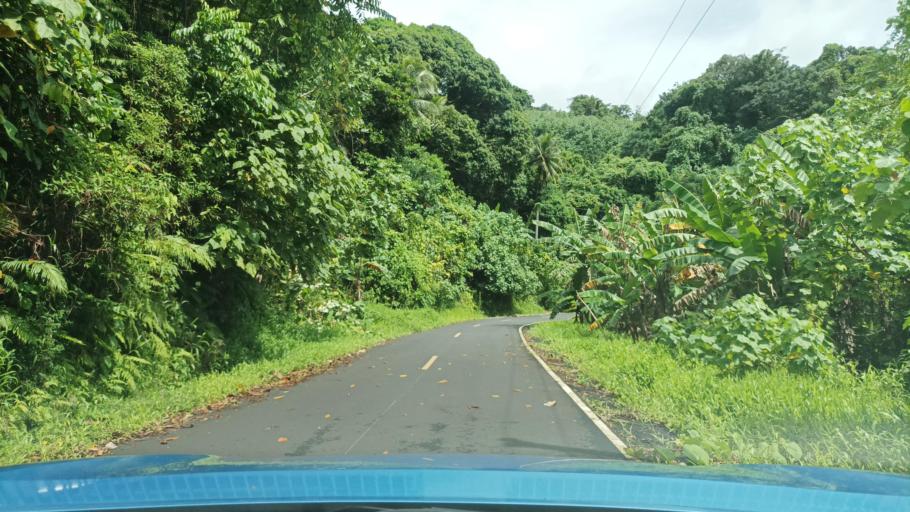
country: FM
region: Pohnpei
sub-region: Madolenihm Municipality
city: Madolenihm Municipality Government
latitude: 6.8706
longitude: 158.3289
